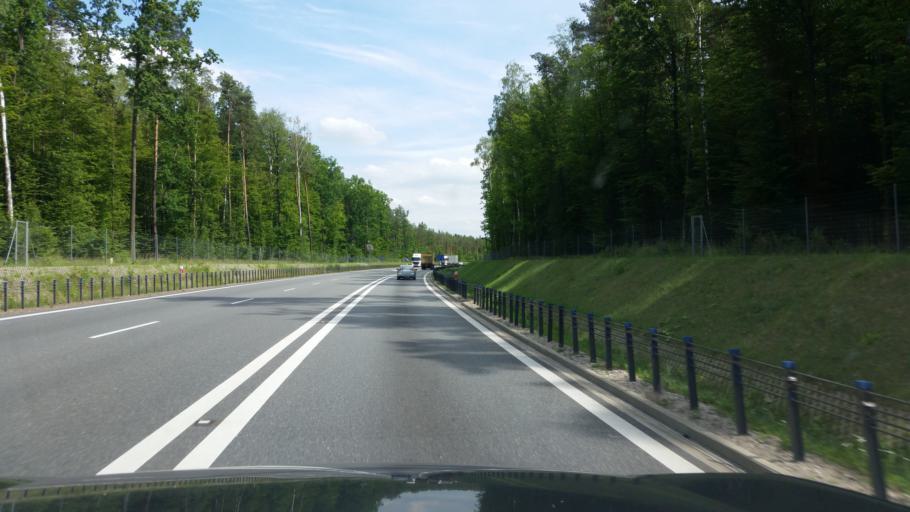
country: PL
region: Masovian Voivodeship
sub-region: Powiat zyrardowski
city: Wiskitki
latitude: 52.0595
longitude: 20.4014
